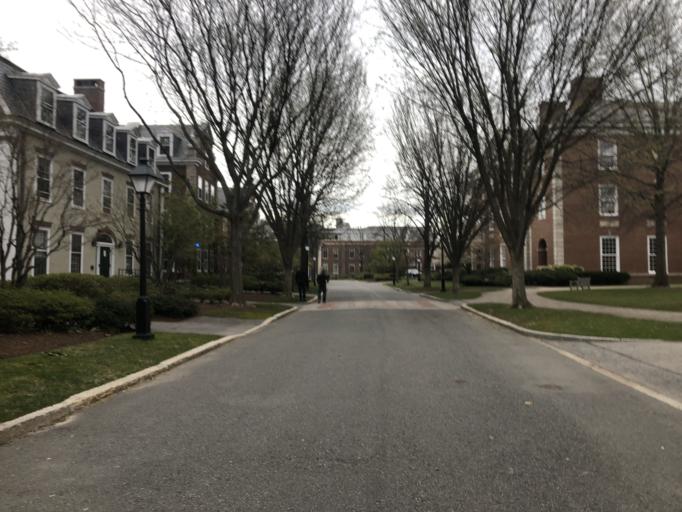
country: US
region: Massachusetts
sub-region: Middlesex County
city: Cambridge
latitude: 42.3666
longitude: -71.1223
